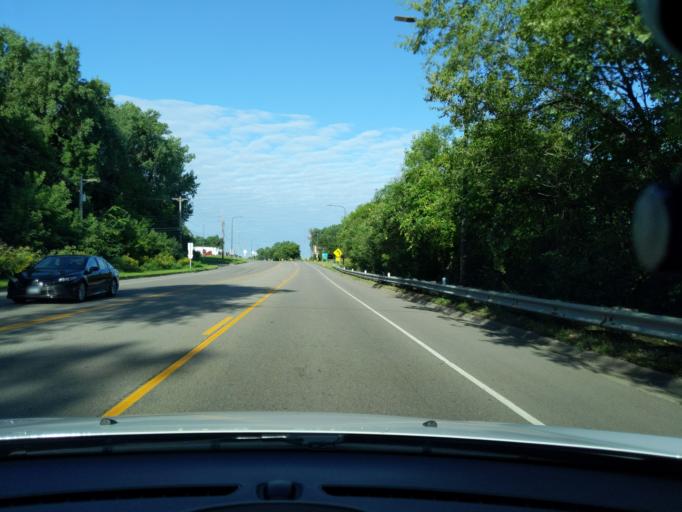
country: US
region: Minnesota
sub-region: Ramsey County
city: Falcon Heights
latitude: 44.9688
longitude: -93.1801
